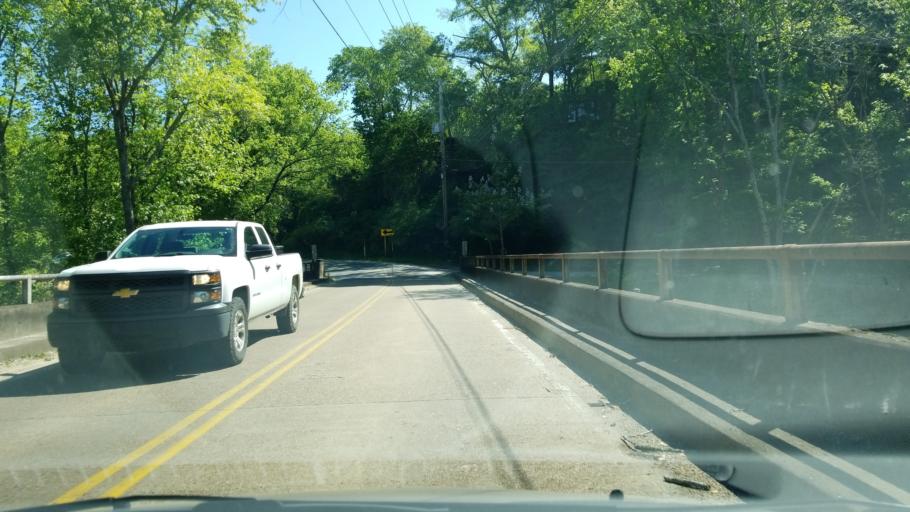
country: US
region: Tennessee
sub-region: Hamilton County
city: Falling Water
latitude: 35.1749
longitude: -85.2280
